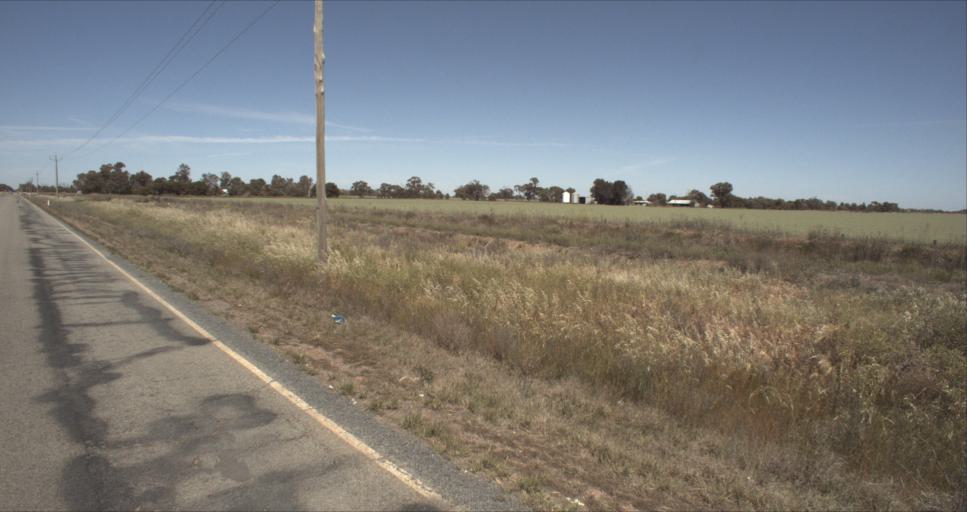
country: AU
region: New South Wales
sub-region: Leeton
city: Leeton
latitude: -34.5104
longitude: 146.2852
